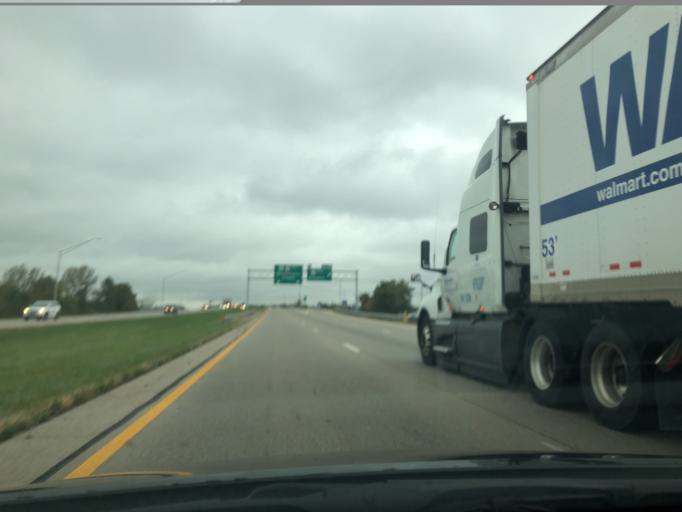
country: US
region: Ohio
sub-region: Union County
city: Marysville
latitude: 40.2354
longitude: -83.3422
